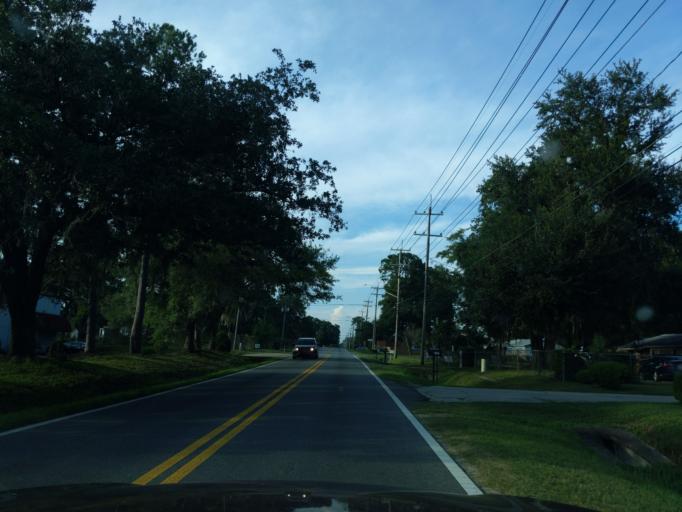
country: US
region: Florida
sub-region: Leon County
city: Tallahassee
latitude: 30.4063
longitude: -84.3062
